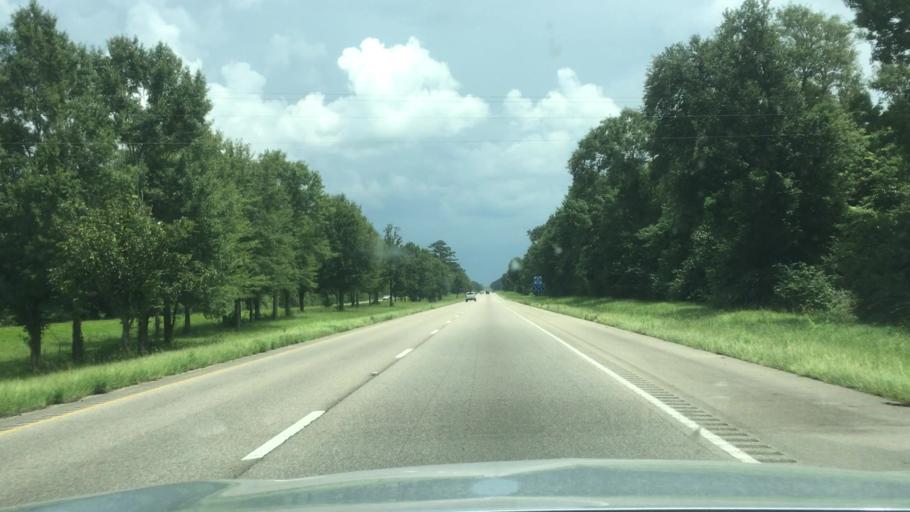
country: US
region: Mississippi
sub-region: Pearl River County
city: Picayune
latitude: 30.5535
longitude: -89.6437
